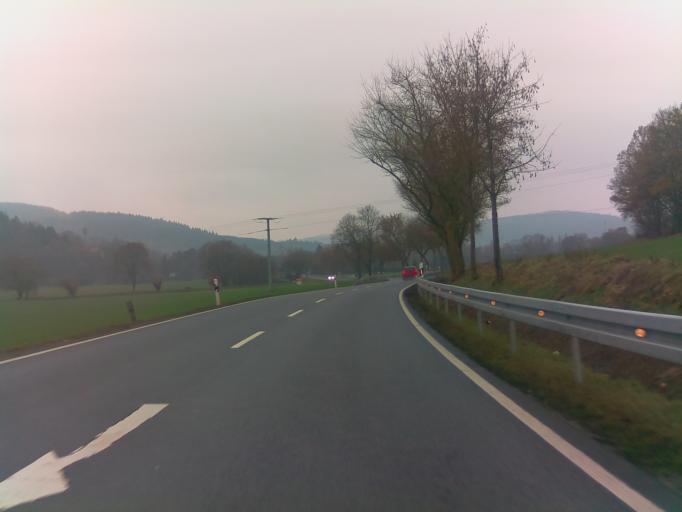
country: DE
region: Thuringia
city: Grimmelshausen
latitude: 50.4926
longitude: 10.6322
